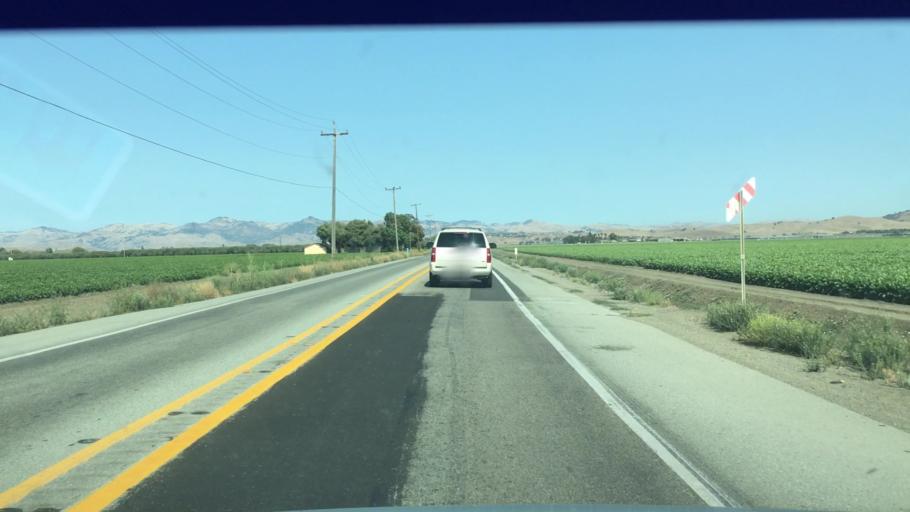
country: US
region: California
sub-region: San Benito County
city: San Juan Bautista
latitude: 36.8411
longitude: -121.5159
